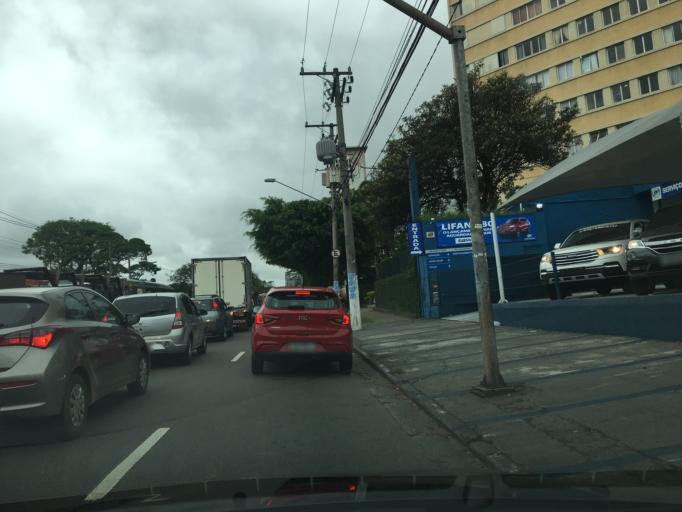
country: BR
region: Sao Paulo
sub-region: Sao Paulo
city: Sao Paulo
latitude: -23.5774
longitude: -46.7080
